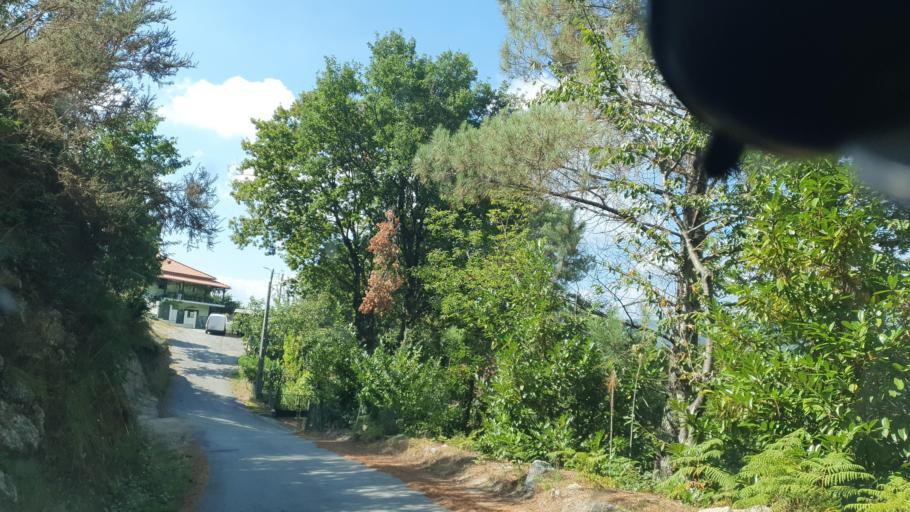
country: PT
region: Braga
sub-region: Vieira do Minho
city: Vieira do Minho
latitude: 41.6744
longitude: -8.1348
